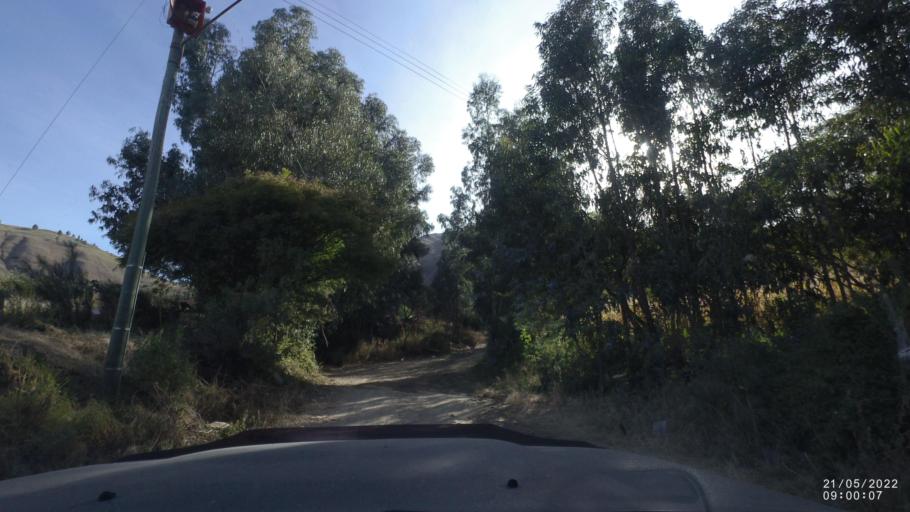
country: BO
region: Cochabamba
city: Cochabamba
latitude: -17.3773
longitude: -66.0360
